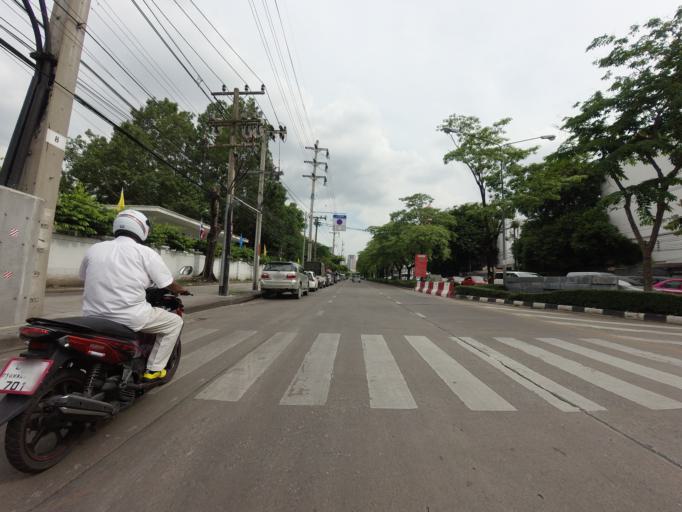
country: TH
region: Bangkok
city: Pathum Wan
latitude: 13.7419
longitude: 100.5354
